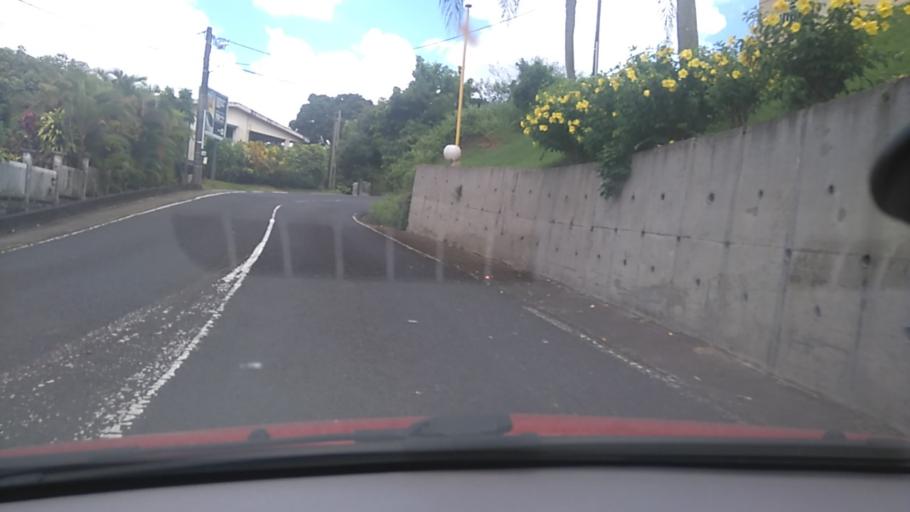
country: MQ
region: Martinique
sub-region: Martinique
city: Ducos
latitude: 14.5720
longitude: -60.9629
